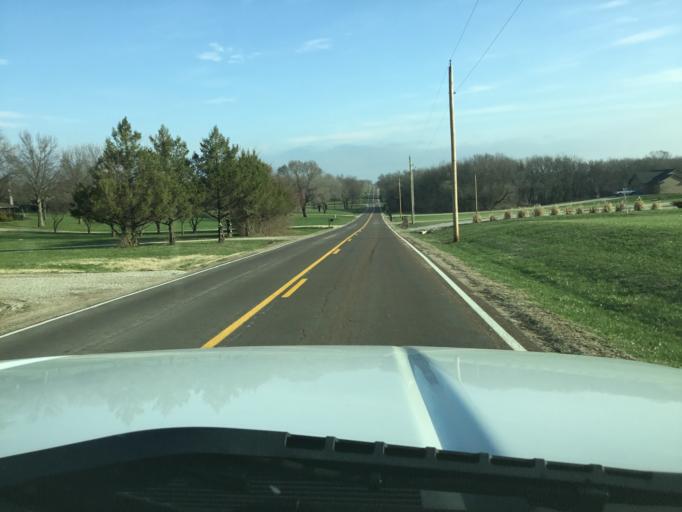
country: US
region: Kansas
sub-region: Shawnee County
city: Topeka
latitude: 39.1128
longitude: -95.7531
